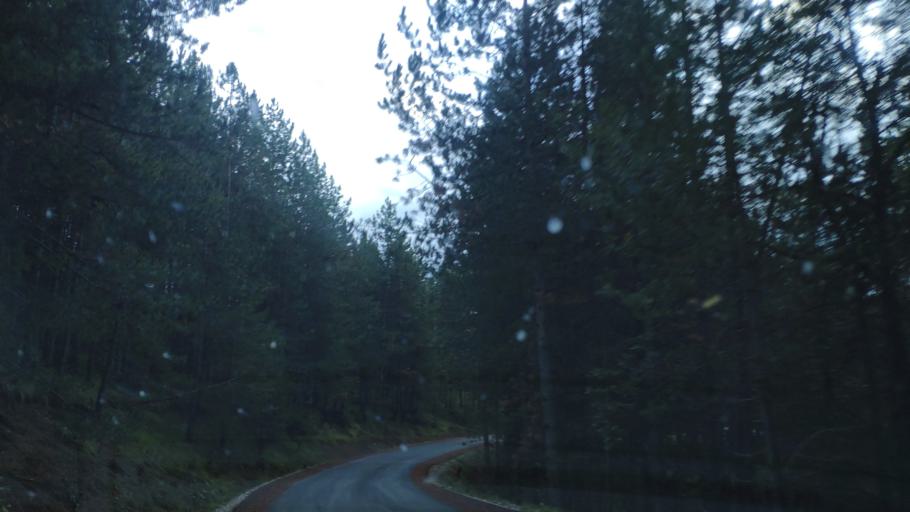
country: AL
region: Korce
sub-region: Rrethi i Kolonjes
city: Erseke
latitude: 40.2915
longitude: 20.8629
